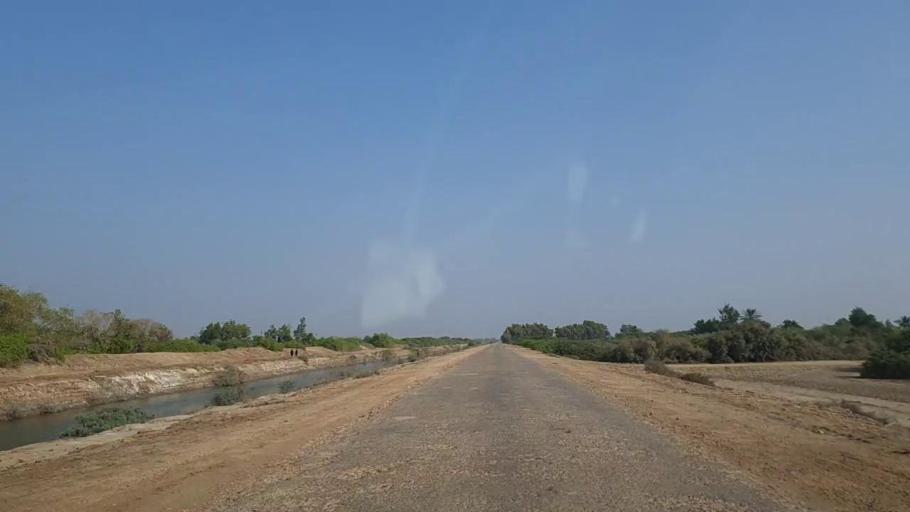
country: PK
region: Sindh
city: Mirpur Sakro
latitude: 24.6323
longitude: 67.6253
